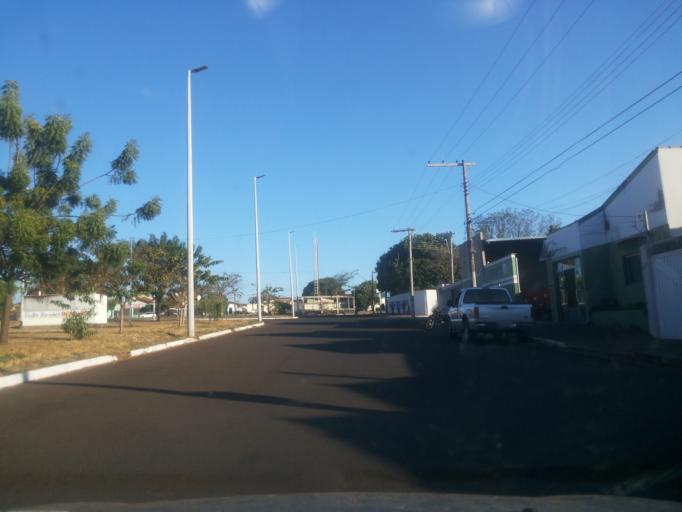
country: BR
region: Minas Gerais
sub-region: Ituiutaba
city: Ituiutaba
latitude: -18.9880
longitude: -49.4619
